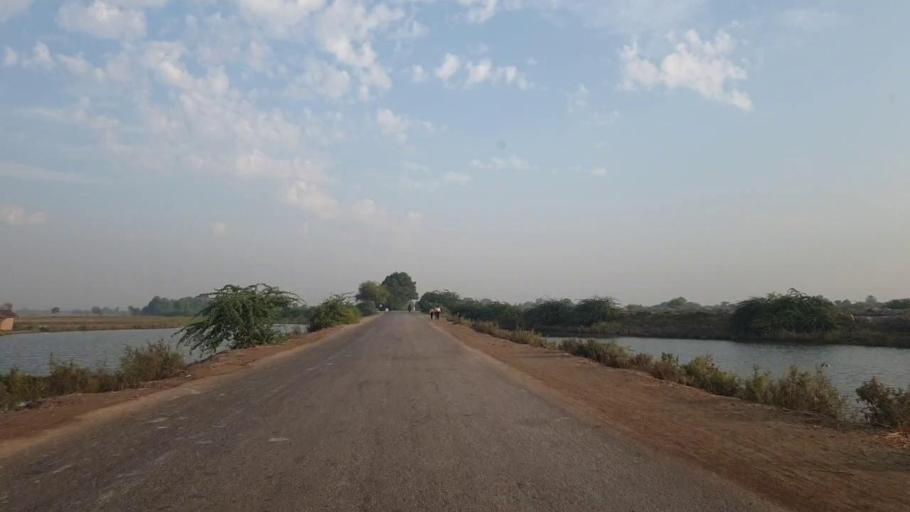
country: PK
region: Sindh
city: Tando Bago
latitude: 24.7137
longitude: 68.9391
